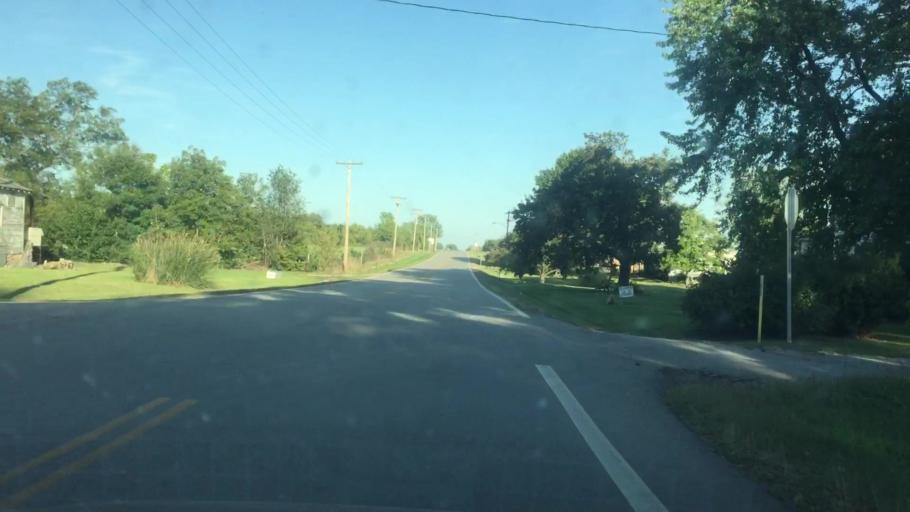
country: US
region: Kansas
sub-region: Brown County
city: Horton
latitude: 39.5876
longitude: -95.6110
